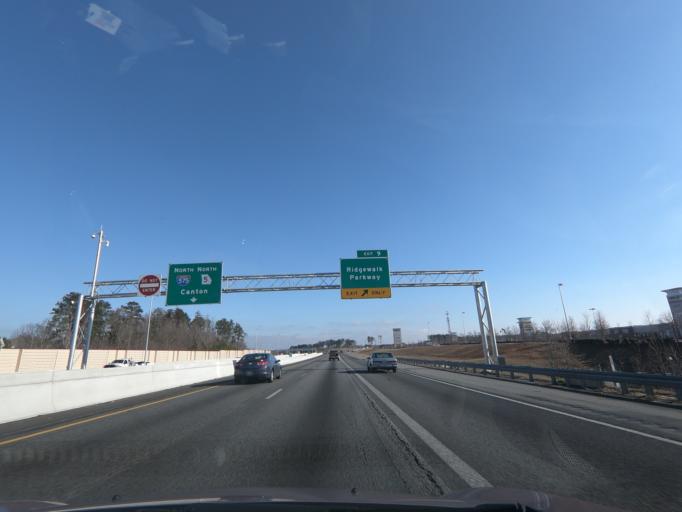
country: US
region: Georgia
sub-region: Cherokee County
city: Woodstock
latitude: 34.1192
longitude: -84.5298
